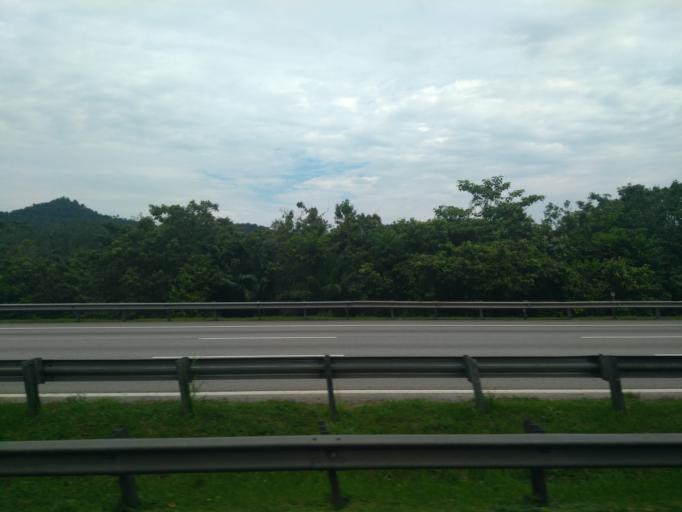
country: MY
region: Negeri Sembilan
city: Tampin
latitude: 2.4665
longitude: 102.1464
